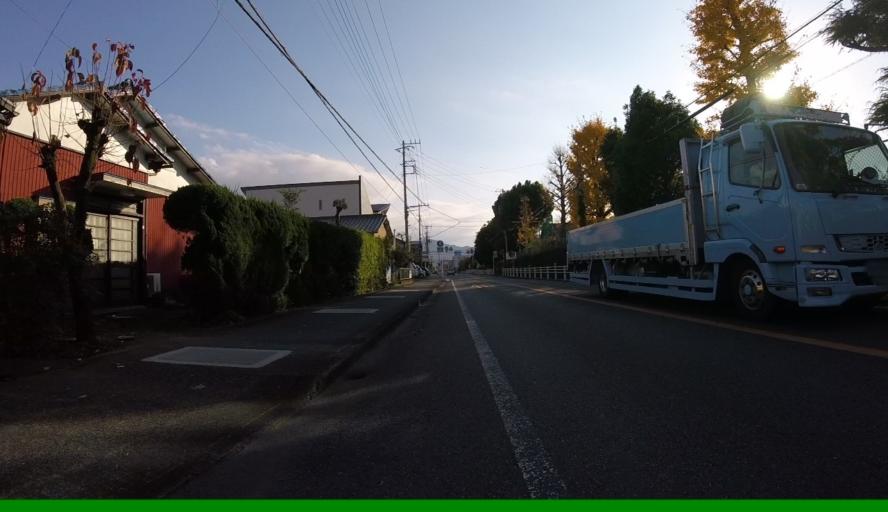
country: JP
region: Shizuoka
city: Mishima
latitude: 35.1016
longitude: 138.9044
